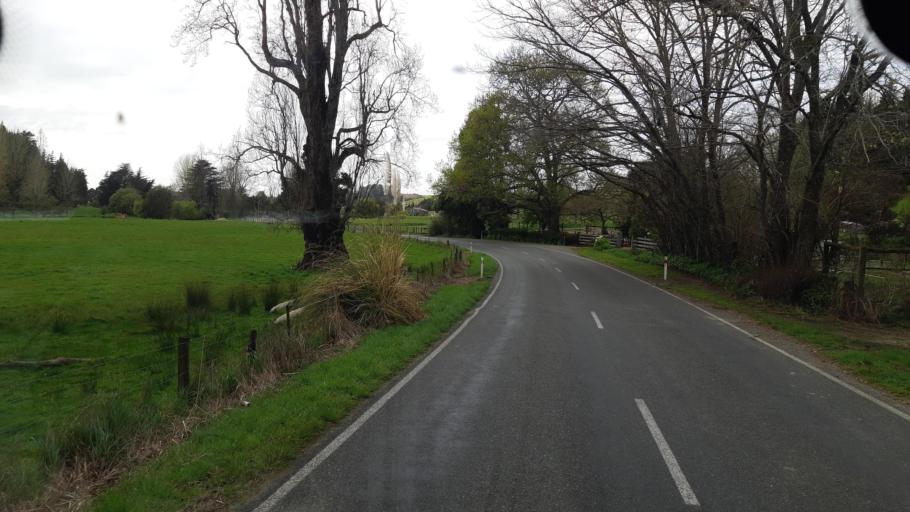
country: NZ
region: Tasman
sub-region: Tasman District
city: Motueka
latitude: -41.2642
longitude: 172.9553
